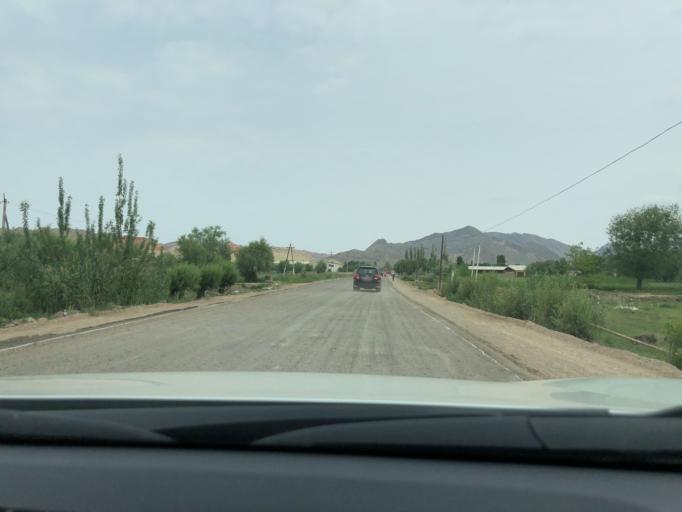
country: TJ
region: Viloyati Sughd
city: Isfara
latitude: 40.1546
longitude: 70.6274
